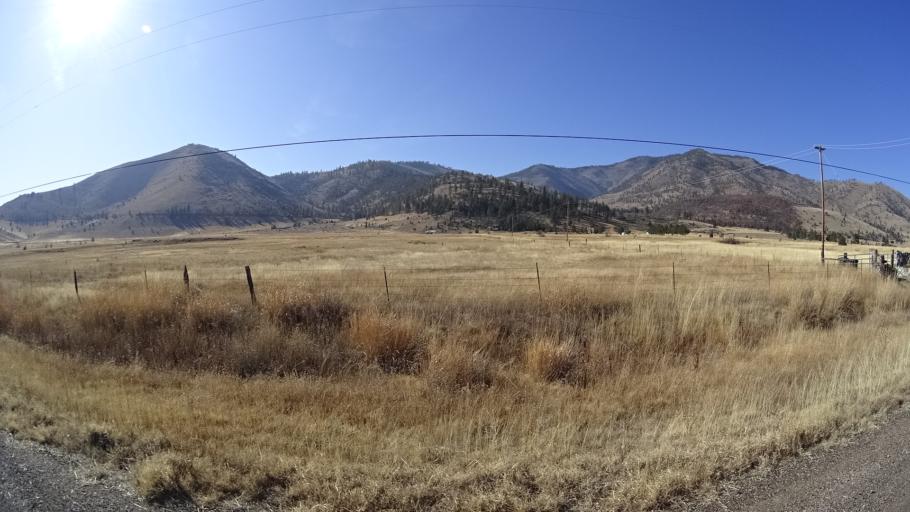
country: US
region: California
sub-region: Siskiyou County
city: Weed
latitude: 41.4741
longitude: -122.4816
